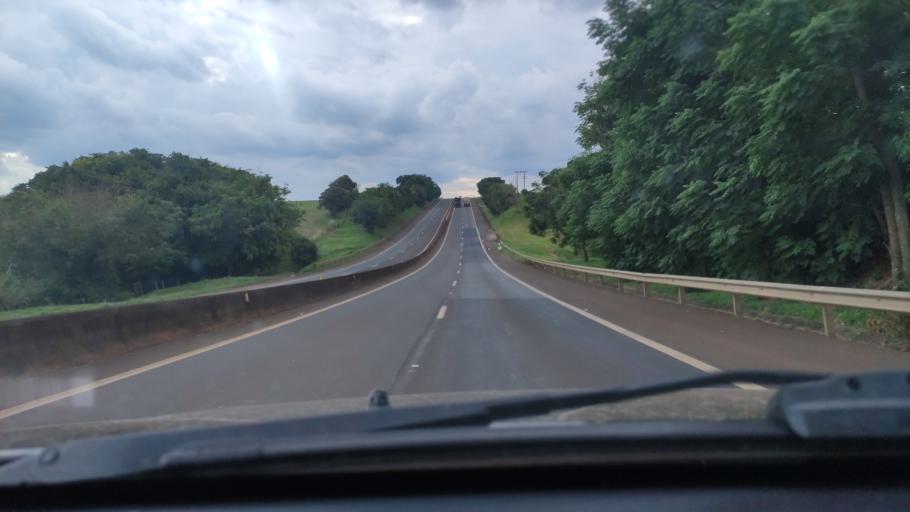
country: BR
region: Sao Paulo
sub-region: Ourinhos
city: Ourinhos
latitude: -22.8417
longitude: -50.0141
